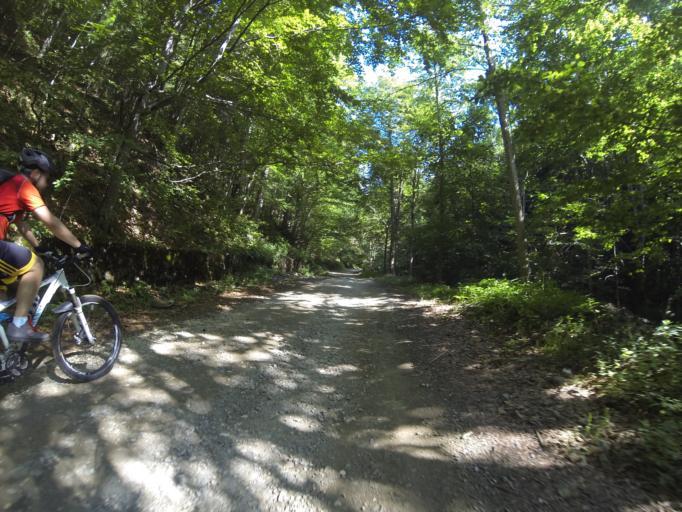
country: RO
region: Valcea
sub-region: Comuna Costesti
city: Bistrita
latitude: 45.2287
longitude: 24.0028
